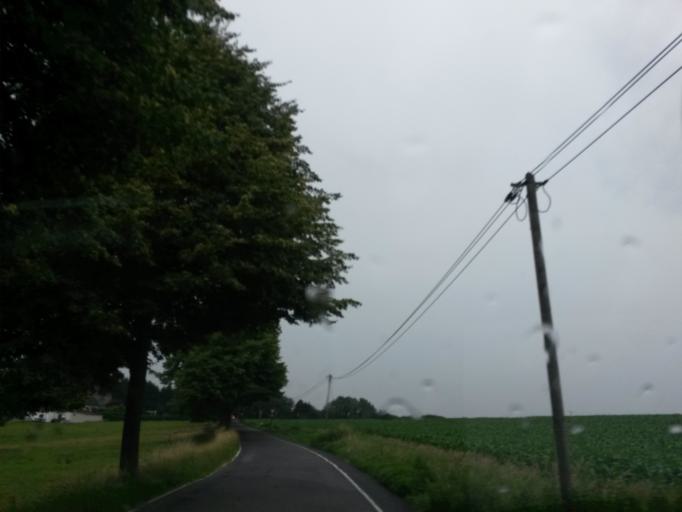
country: DE
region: North Rhine-Westphalia
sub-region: Regierungsbezirk Koln
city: Much
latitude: 50.9387
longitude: 7.3590
